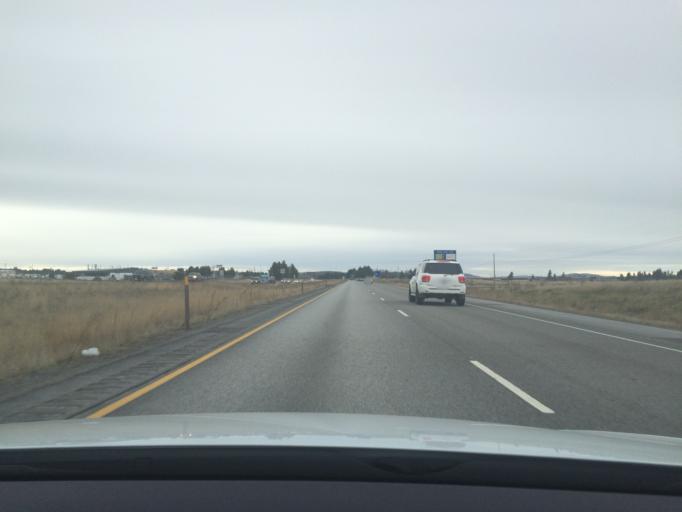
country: US
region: Washington
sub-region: Spokane County
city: Airway Heights
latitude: 47.5984
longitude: -117.5530
